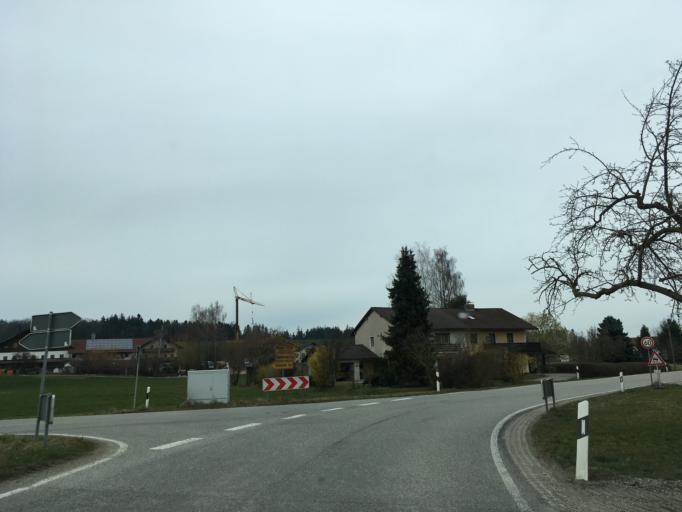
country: DE
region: Bavaria
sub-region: Upper Bavaria
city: Schnaitsee
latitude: 48.0738
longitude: 12.3916
